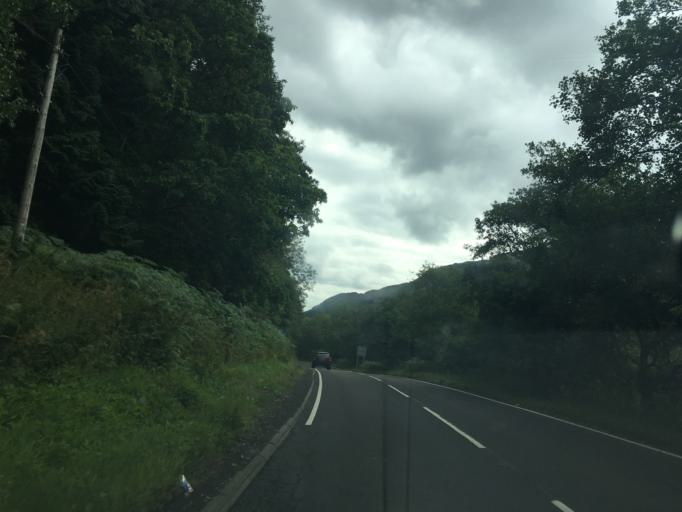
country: GB
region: Scotland
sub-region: Stirling
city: Callander
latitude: 56.3067
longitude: -4.3224
